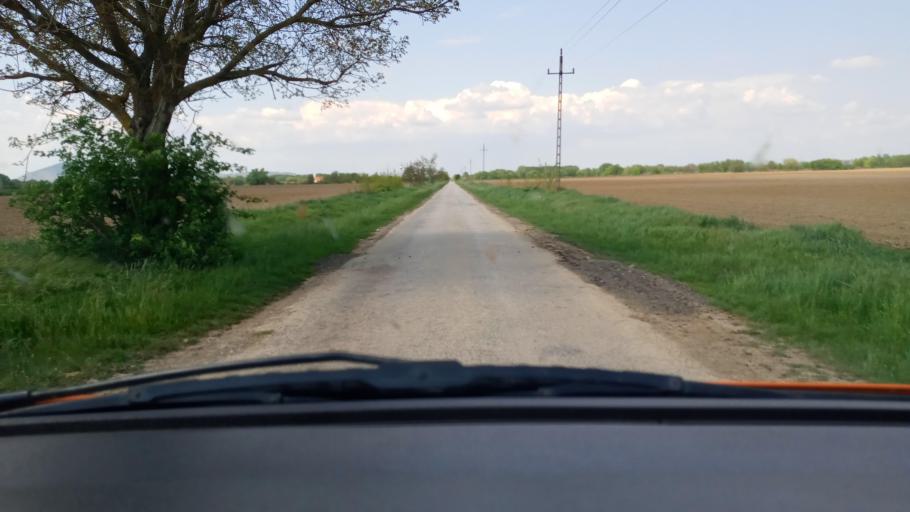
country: HU
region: Baranya
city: Beremend
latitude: 45.8102
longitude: 18.5150
